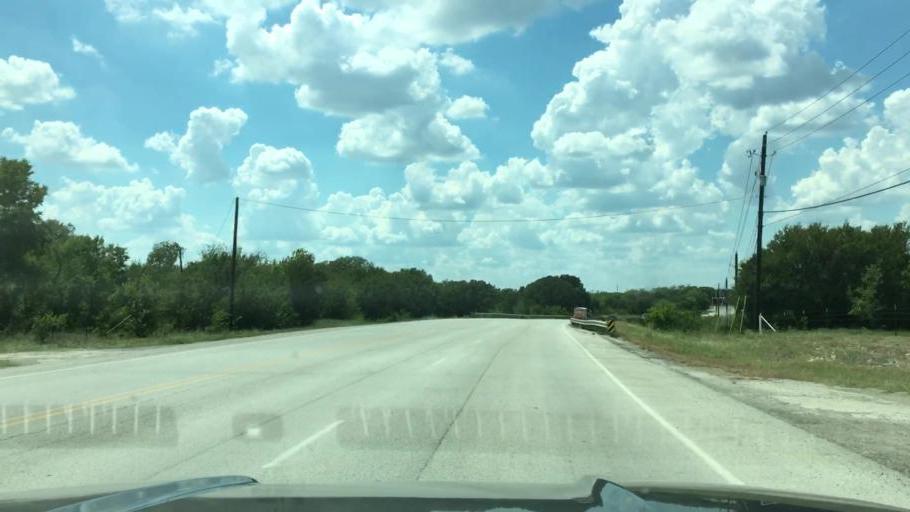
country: US
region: Texas
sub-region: Tarrant County
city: Haslet
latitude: 32.9742
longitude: -97.3415
